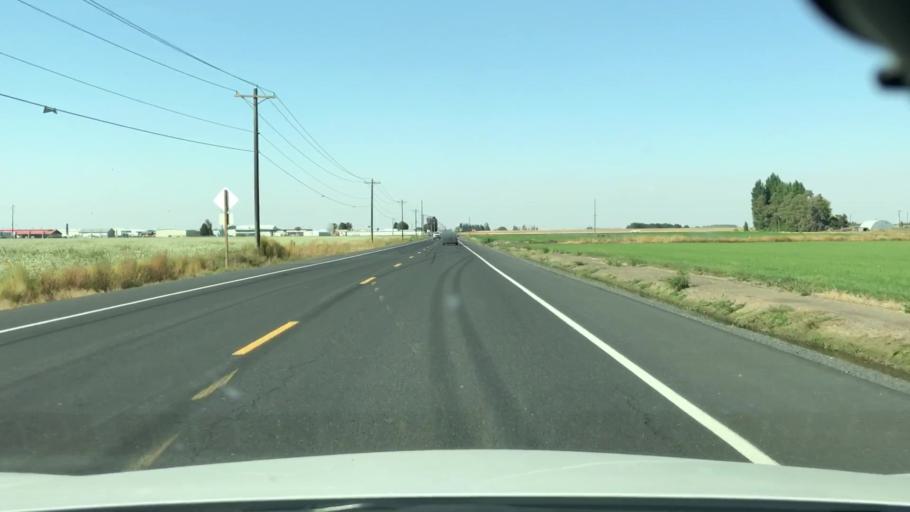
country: US
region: Washington
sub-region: Grant County
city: Moses Lake
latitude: 47.1268
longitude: -119.2358
